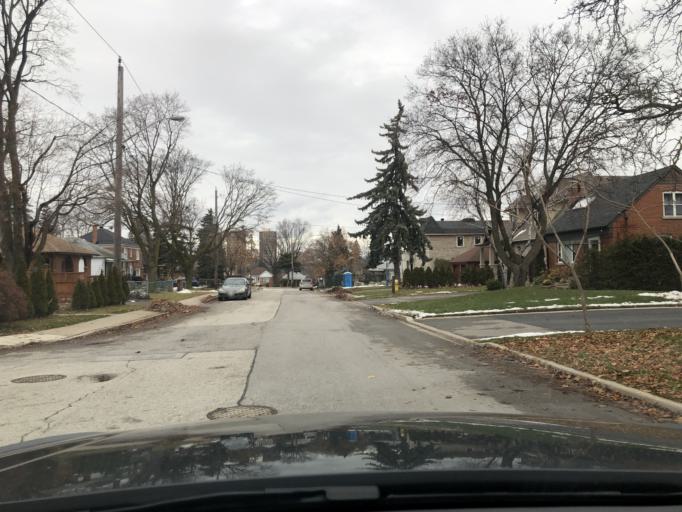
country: CA
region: Ontario
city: Etobicoke
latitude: 43.6993
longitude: -79.5301
